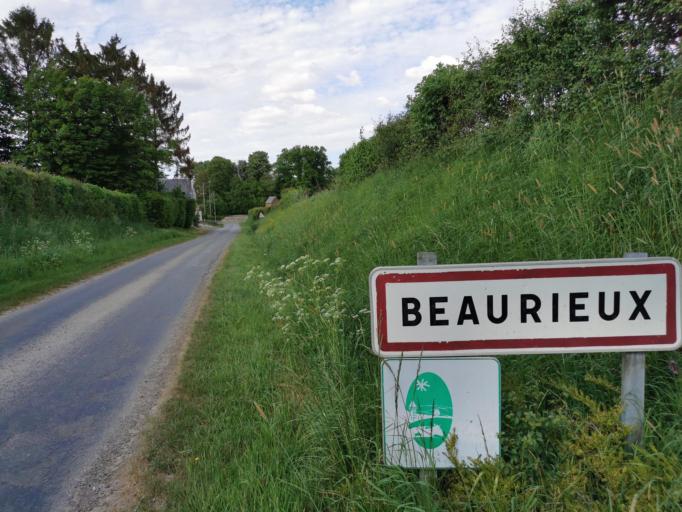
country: FR
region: Nord-Pas-de-Calais
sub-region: Departement du Nord
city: Trelon
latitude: 50.1746
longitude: 4.1268
